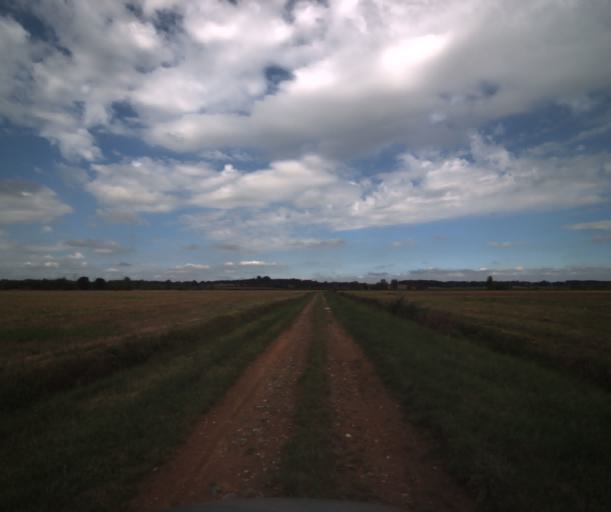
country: FR
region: Midi-Pyrenees
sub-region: Departement de la Haute-Garonne
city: Lherm
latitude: 43.3962
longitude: 1.2313
